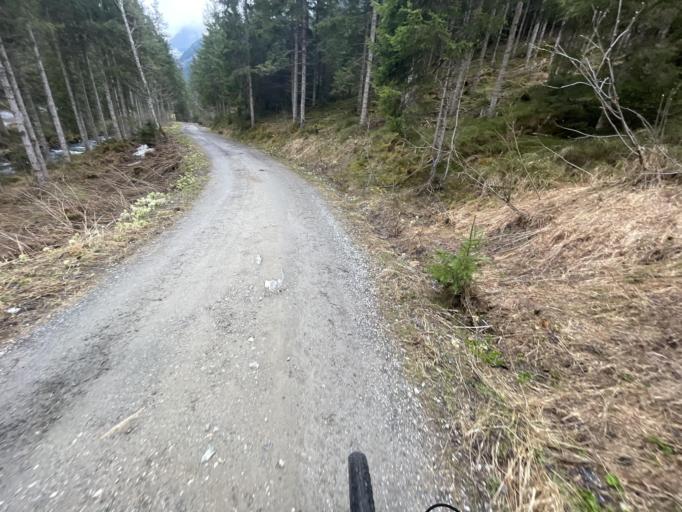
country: AT
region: Styria
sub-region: Politischer Bezirk Liezen
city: Schladming
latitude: 47.3436
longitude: 13.7317
